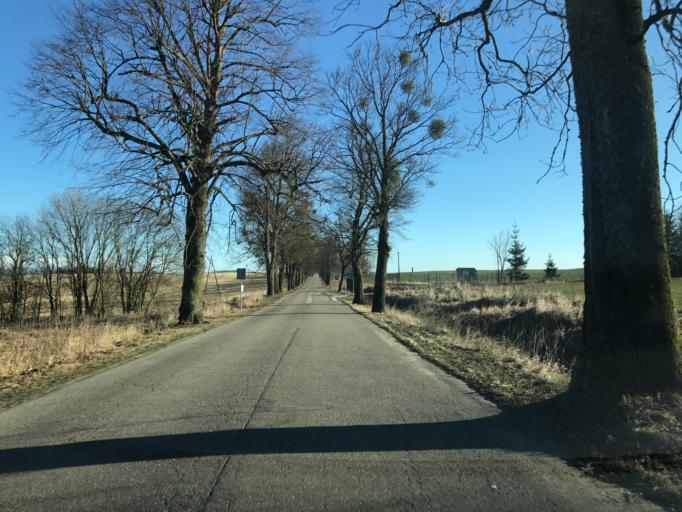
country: PL
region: Warmian-Masurian Voivodeship
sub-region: Powiat olsztynski
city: Jonkowo
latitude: 53.9347
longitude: 20.2792
